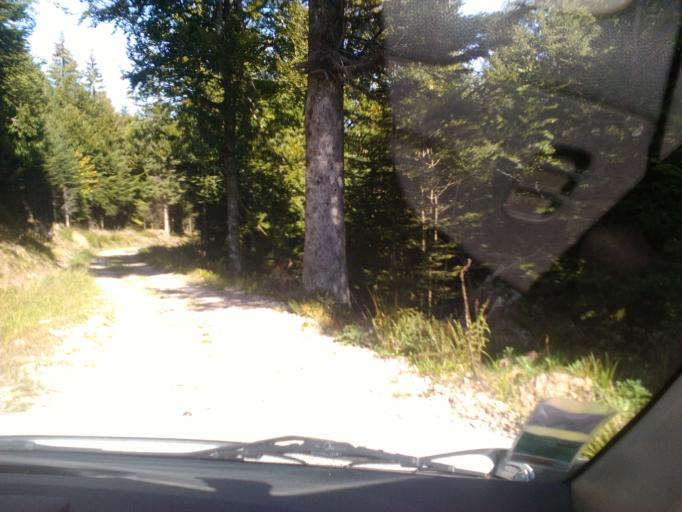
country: FR
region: Lorraine
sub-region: Departement des Vosges
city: Le Tholy
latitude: 48.0470
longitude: 6.7798
